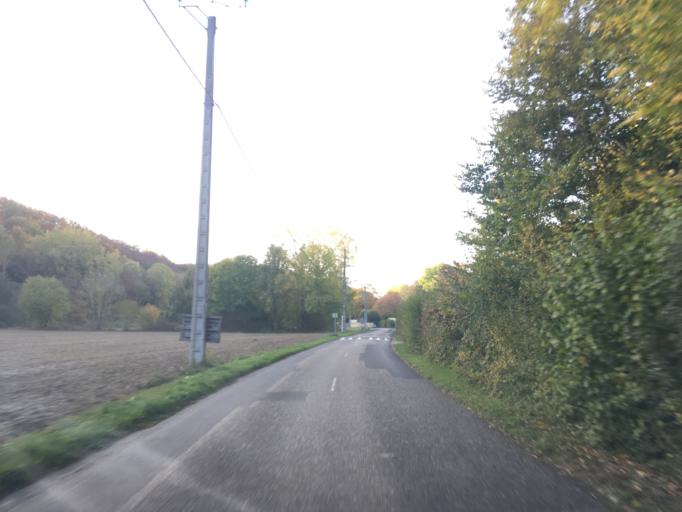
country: FR
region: Haute-Normandie
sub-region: Departement de l'Eure
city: Heudreville-sur-Eure
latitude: 49.1016
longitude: 1.2362
